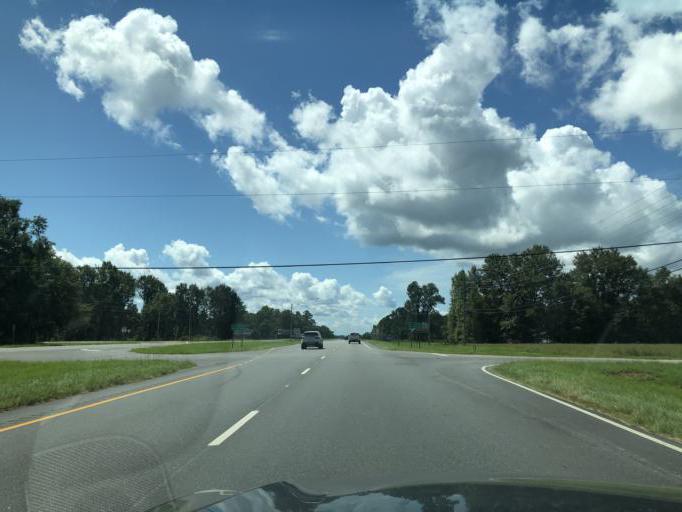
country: US
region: Alabama
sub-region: Barbour County
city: Eufaula
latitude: 32.0019
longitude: -85.1161
